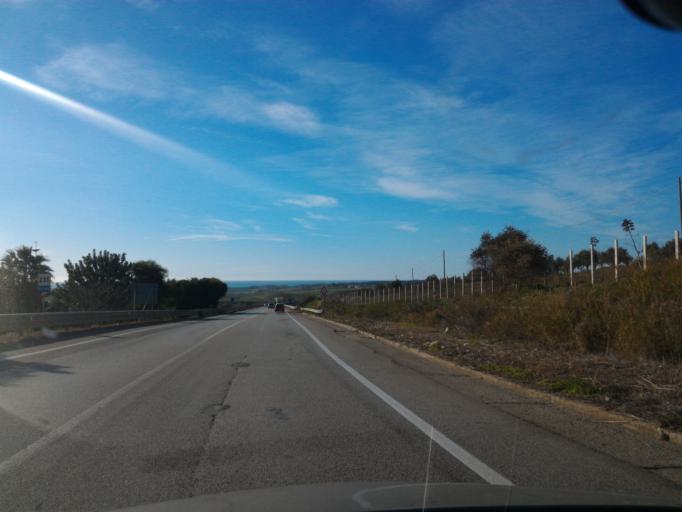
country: IT
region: Calabria
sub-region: Provincia di Crotone
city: Isola di Capo Rizzuto
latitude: 38.9476
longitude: 17.0825
